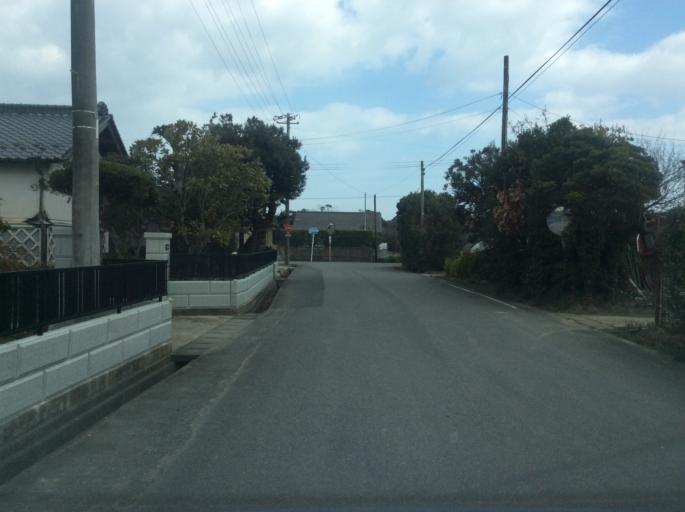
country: JP
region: Fukushima
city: Iwaki
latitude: 37.0771
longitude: 140.9686
